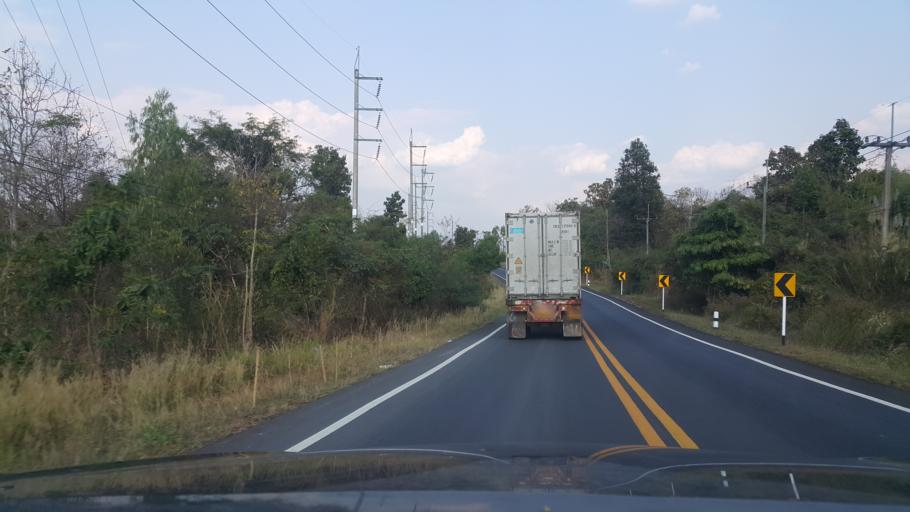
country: TH
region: Phitsanulok
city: Nakhon Thai
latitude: 17.1381
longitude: 100.9348
